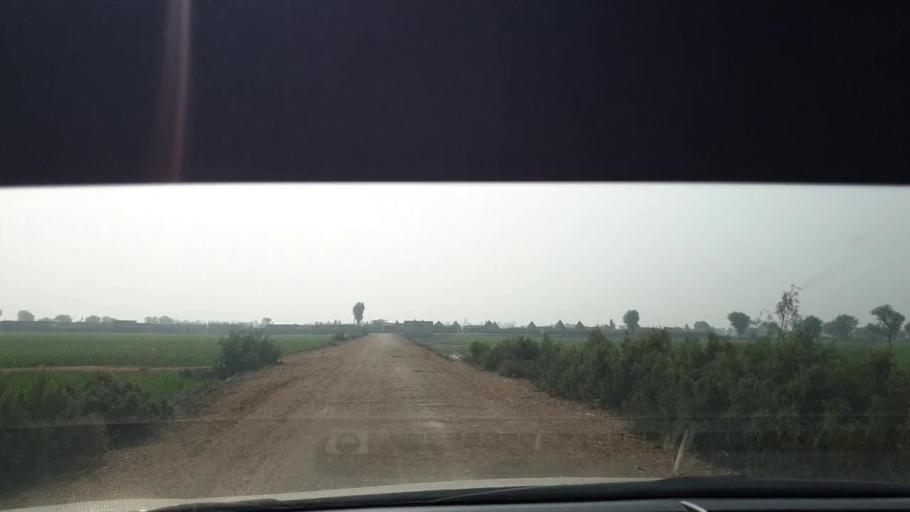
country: PK
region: Sindh
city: Berani
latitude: 25.7724
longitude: 68.8007
